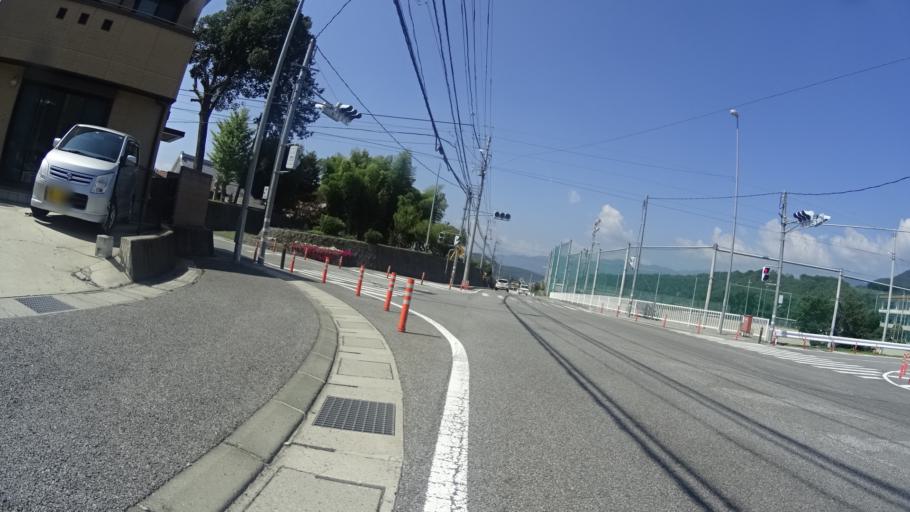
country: JP
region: Yamanashi
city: Enzan
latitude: 35.7222
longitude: 138.7524
